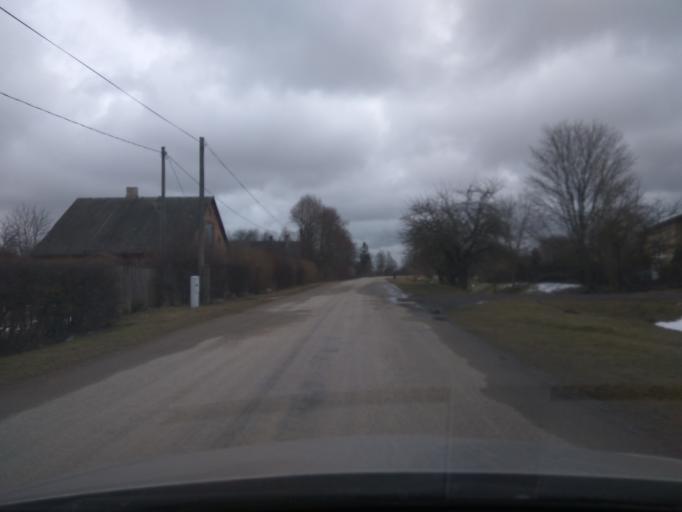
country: LV
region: Ventspils
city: Ventspils
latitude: 57.3323
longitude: 21.6500
